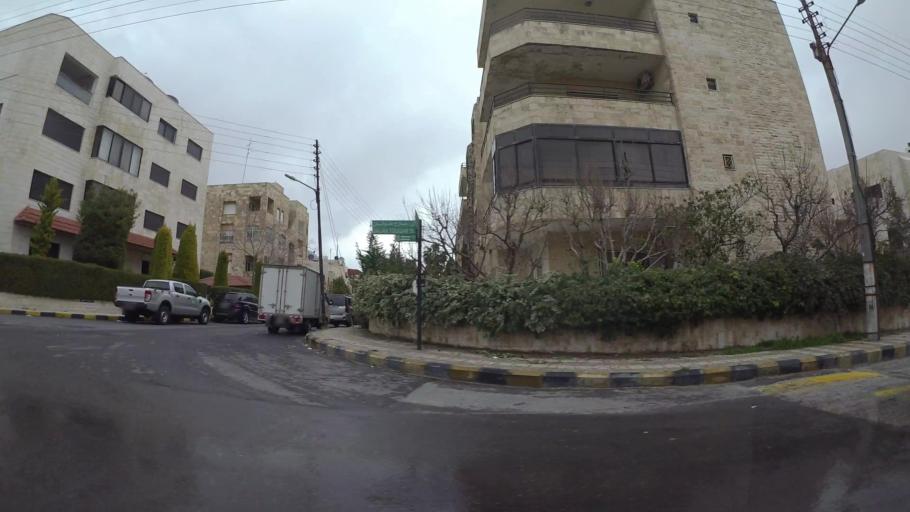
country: JO
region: Amman
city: Wadi as Sir
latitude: 31.9518
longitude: 35.8681
